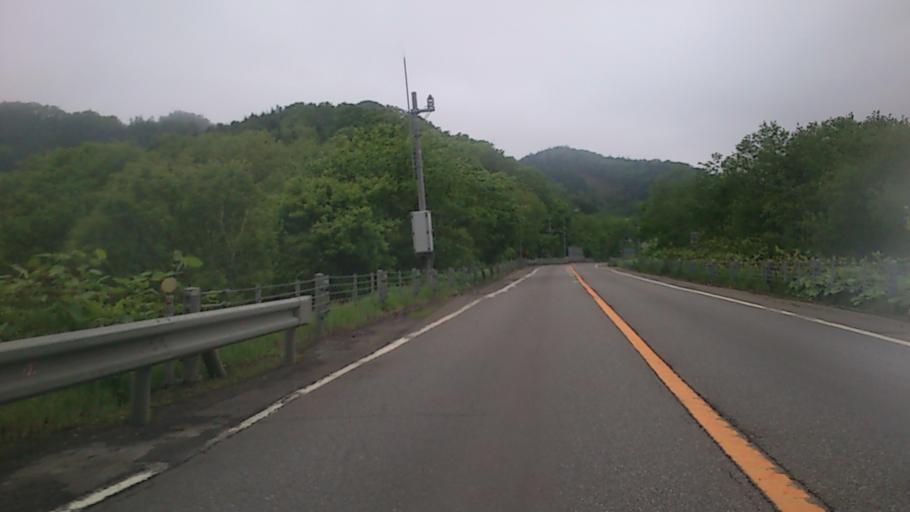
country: JP
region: Hokkaido
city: Obihiro
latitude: 42.8376
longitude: 143.7761
